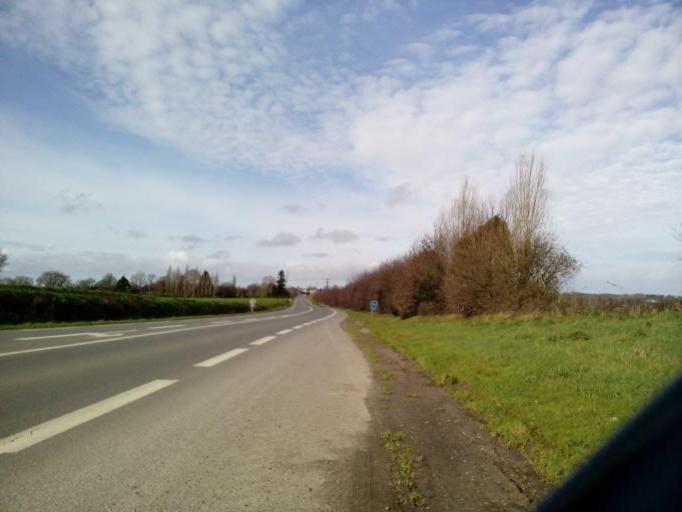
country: FR
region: Brittany
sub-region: Departement d'Ille-et-Vilaine
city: Montgermont
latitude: 48.1621
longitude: -1.7121
